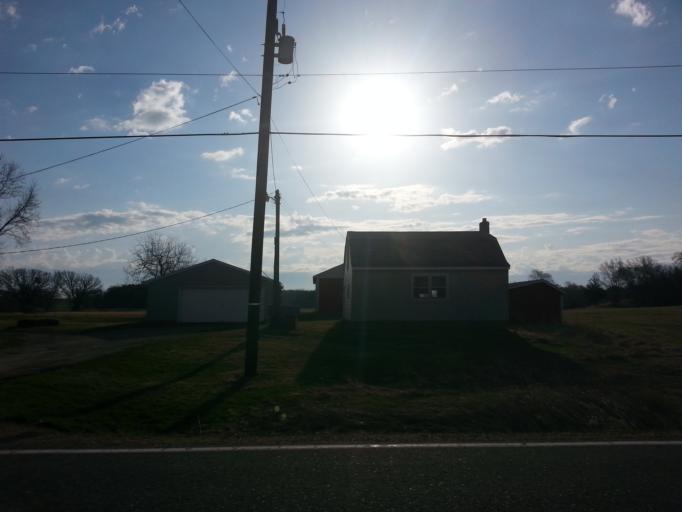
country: US
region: Minnesota
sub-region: Washington County
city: Afton
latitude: 44.9148
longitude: -92.8428
